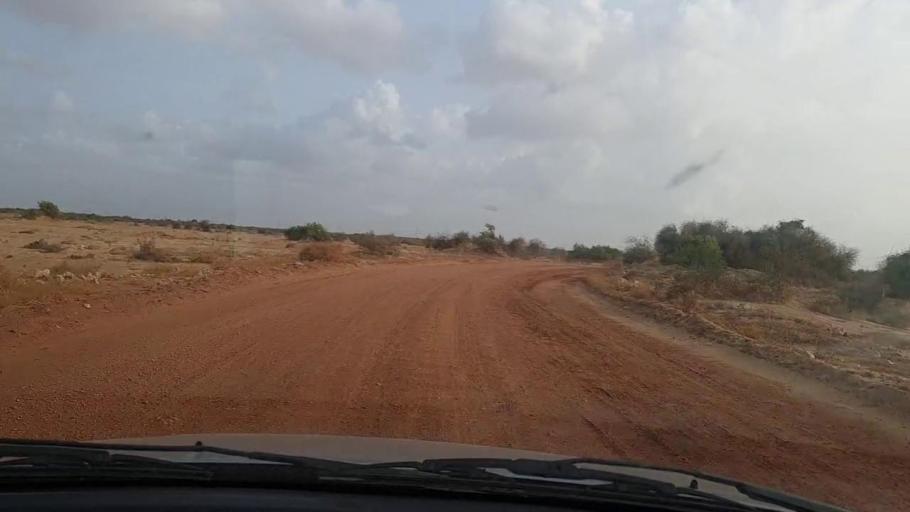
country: PK
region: Sindh
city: Thatta
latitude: 25.0681
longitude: 67.8896
